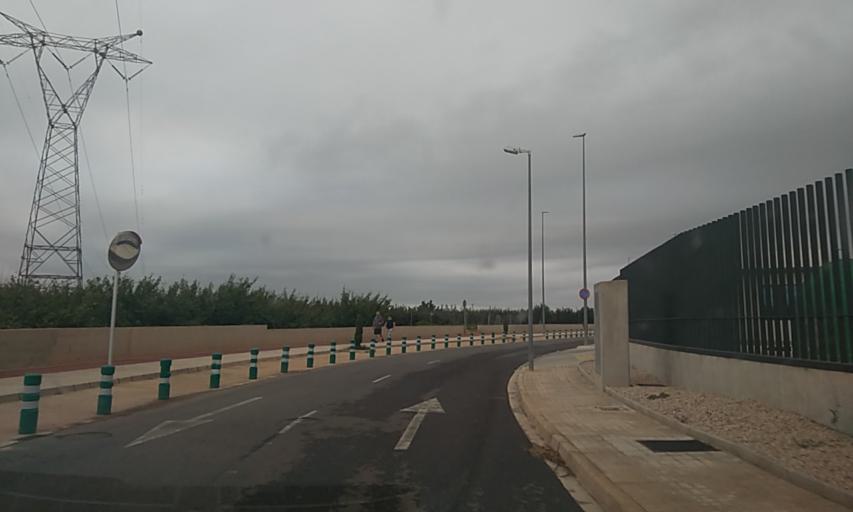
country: ES
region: Valencia
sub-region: Provincia de Valencia
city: L'Alcudia
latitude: 39.1932
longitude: -0.5170
